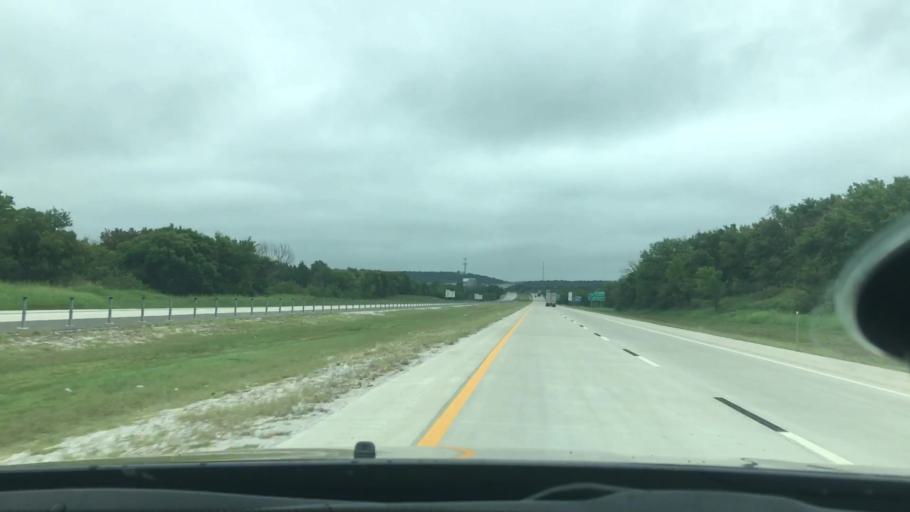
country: US
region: Oklahoma
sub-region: Okmulgee County
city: Henryetta
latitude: 35.4339
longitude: -96.0030
